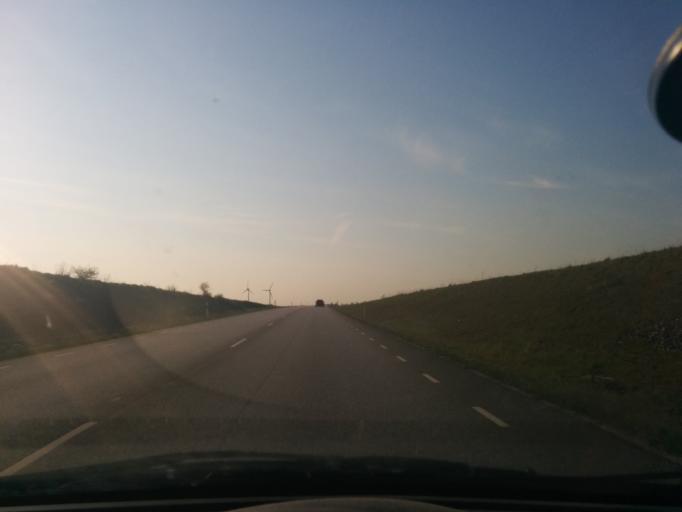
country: SE
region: Skane
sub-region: Staffanstorps Kommun
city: Hjaerup
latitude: 55.6866
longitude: 13.1554
